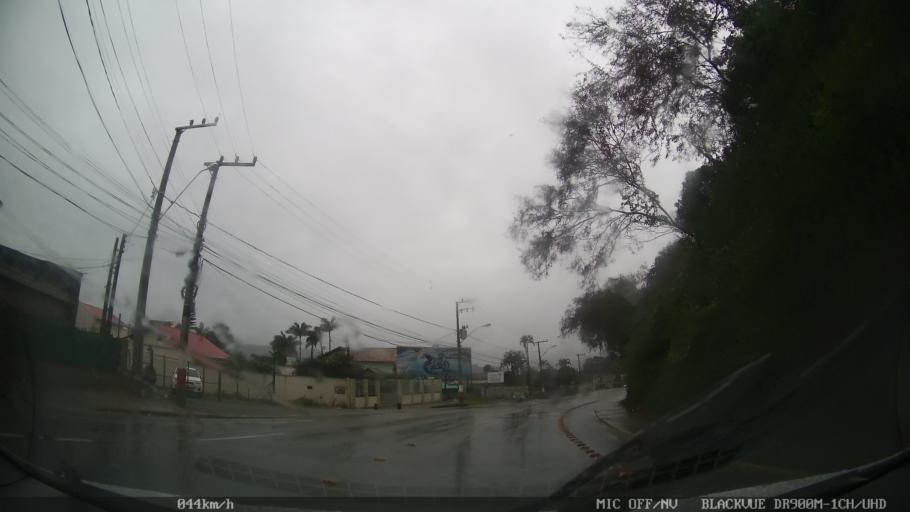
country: BR
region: Santa Catarina
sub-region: Balneario Camboriu
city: Balneario Camboriu
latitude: -27.0119
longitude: -48.6479
